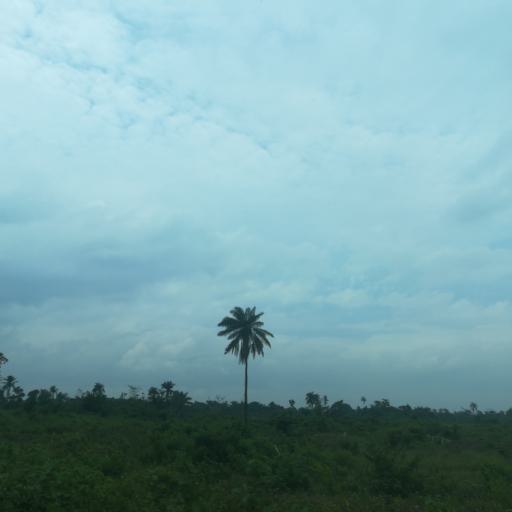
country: NG
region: Lagos
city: Ejirin
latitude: 6.6470
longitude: 3.7610
